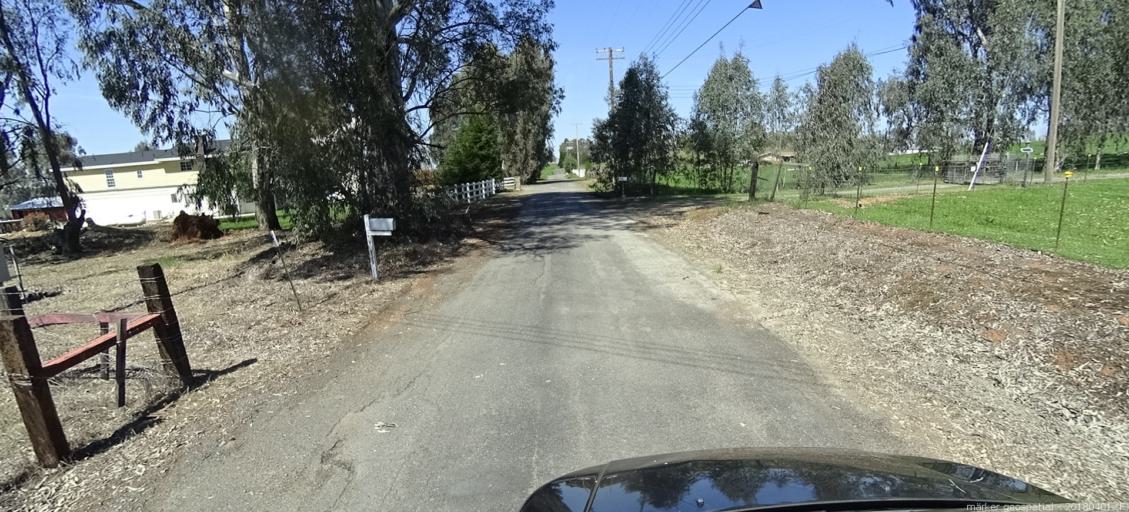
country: US
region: California
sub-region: Sacramento County
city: Wilton
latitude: 38.3886
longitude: -121.2285
